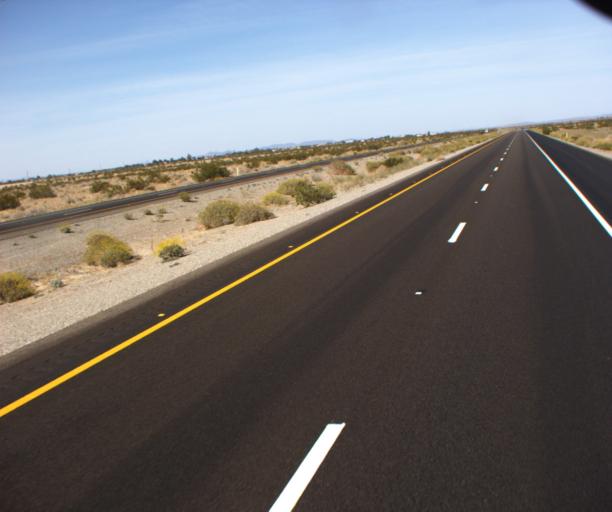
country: US
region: Arizona
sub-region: Yuma County
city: Fortuna Foothills
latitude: 32.5841
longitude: -114.5508
